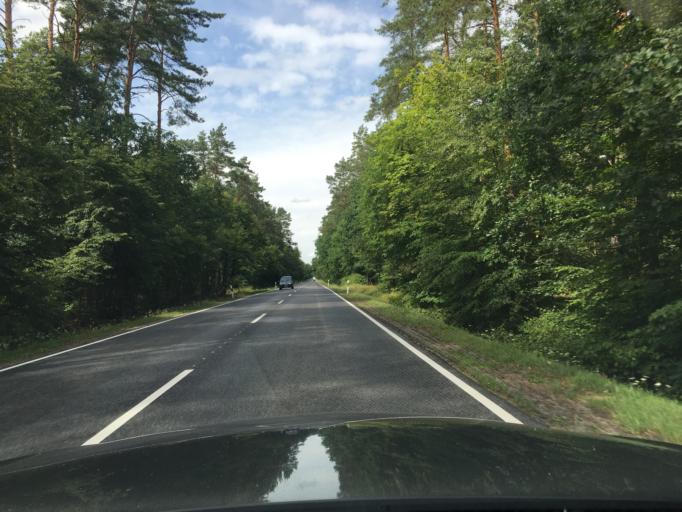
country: DE
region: Brandenburg
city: Furstenberg
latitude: 53.2036
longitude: 13.1338
